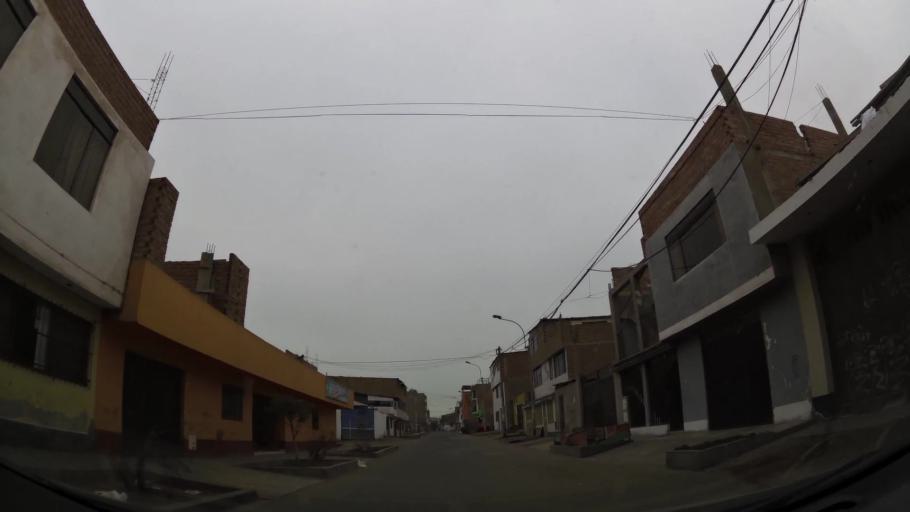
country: PE
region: Lima
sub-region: Lima
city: Surco
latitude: -12.1819
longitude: -76.9779
